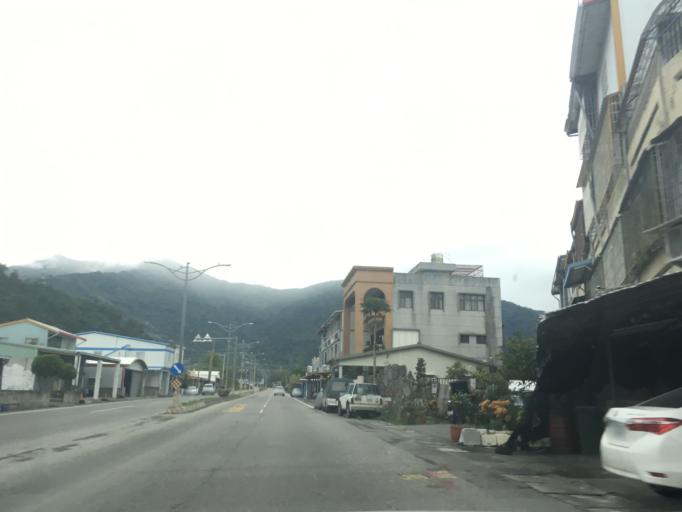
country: TW
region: Taiwan
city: Taitung City
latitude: 22.6949
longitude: 121.0454
